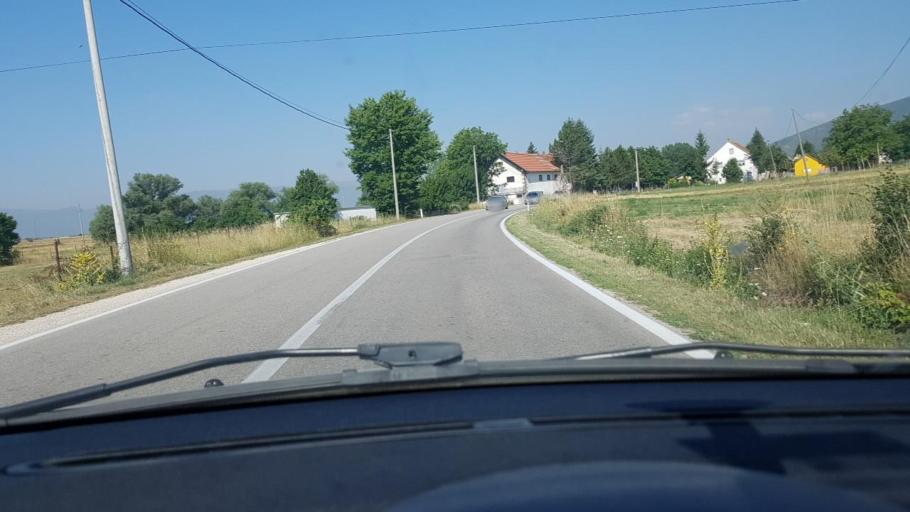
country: BA
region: Federation of Bosnia and Herzegovina
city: Zabrisce
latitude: 43.8538
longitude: 16.9472
